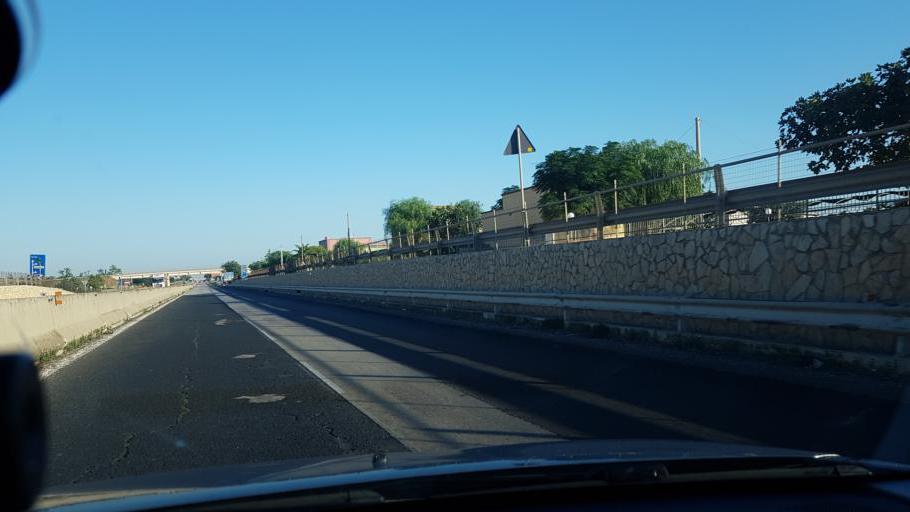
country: IT
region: Apulia
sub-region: Provincia di Brindisi
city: Fasano
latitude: 40.8691
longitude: 17.3441
